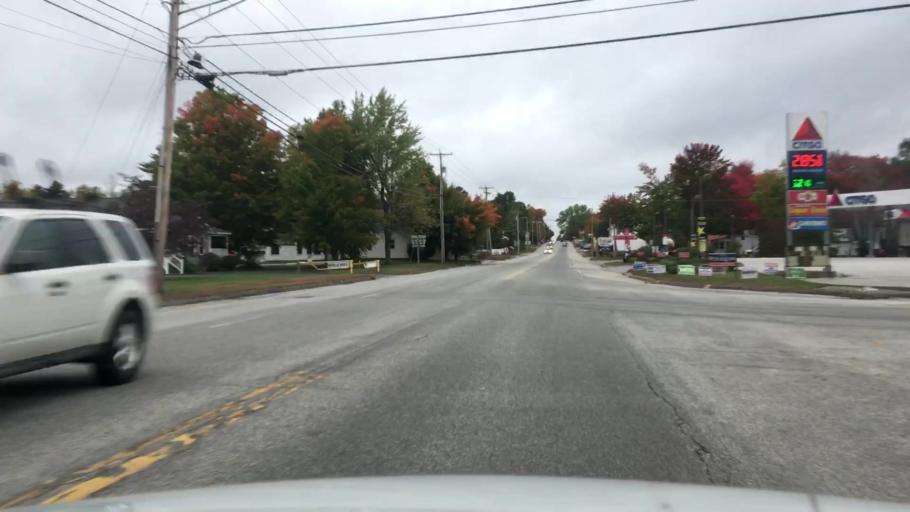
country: US
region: Maine
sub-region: Oxford County
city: Oxford
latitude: 44.1335
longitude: -70.4638
